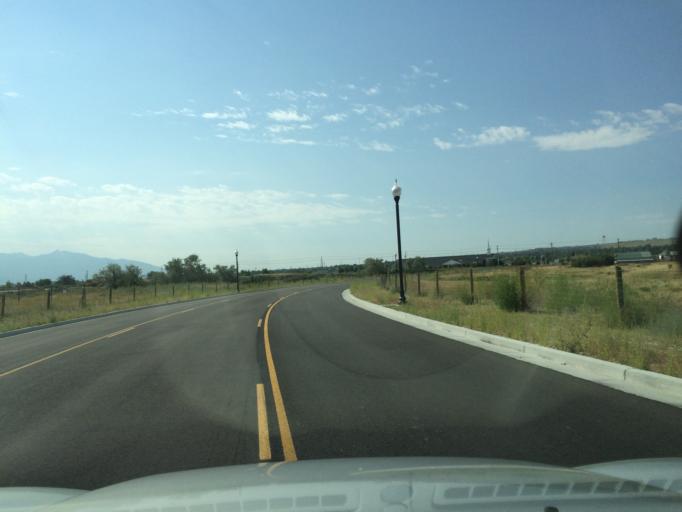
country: US
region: Utah
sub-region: Salt Lake County
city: West Valley City
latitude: 40.7132
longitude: -112.0446
